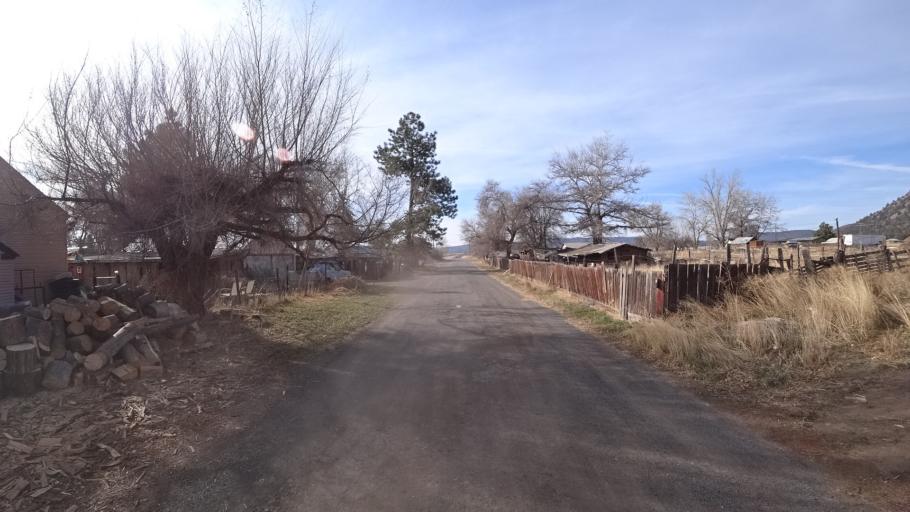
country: US
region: Oregon
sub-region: Klamath County
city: Klamath Falls
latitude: 41.9716
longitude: -121.9199
